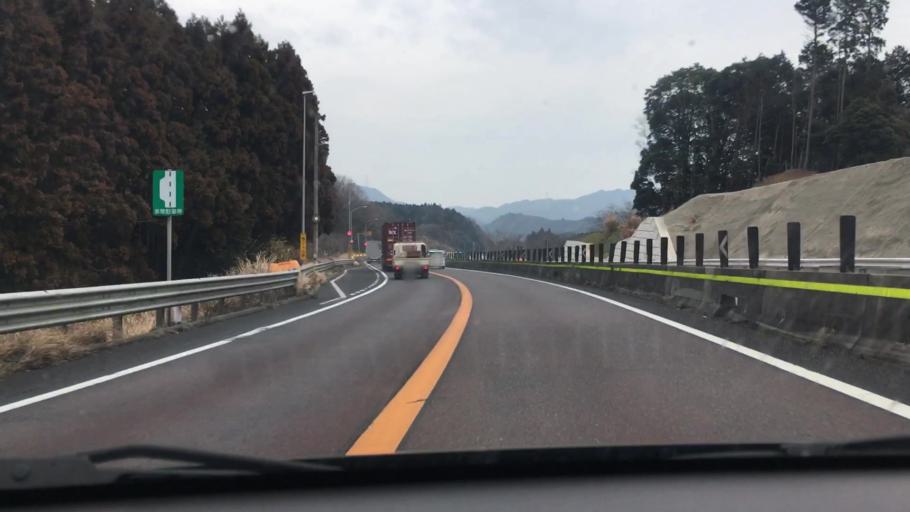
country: JP
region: Mie
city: Kameyama
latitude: 34.8345
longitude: 136.2951
